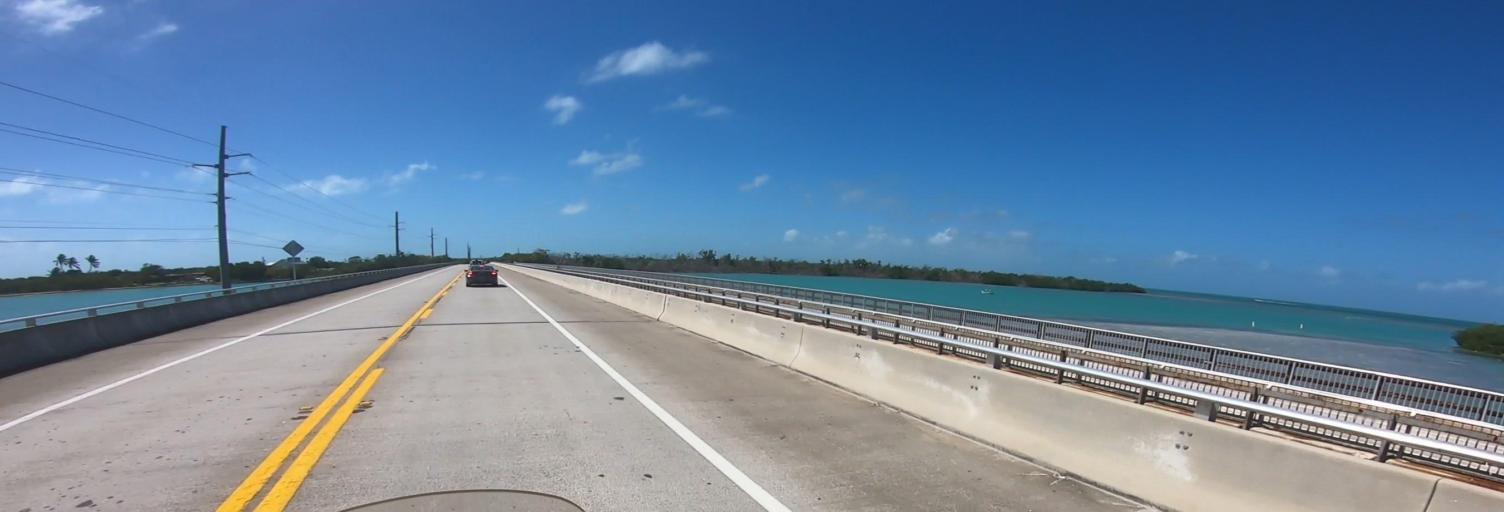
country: US
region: Florida
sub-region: Monroe County
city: Big Pine Key
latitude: 24.6708
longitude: -81.2484
